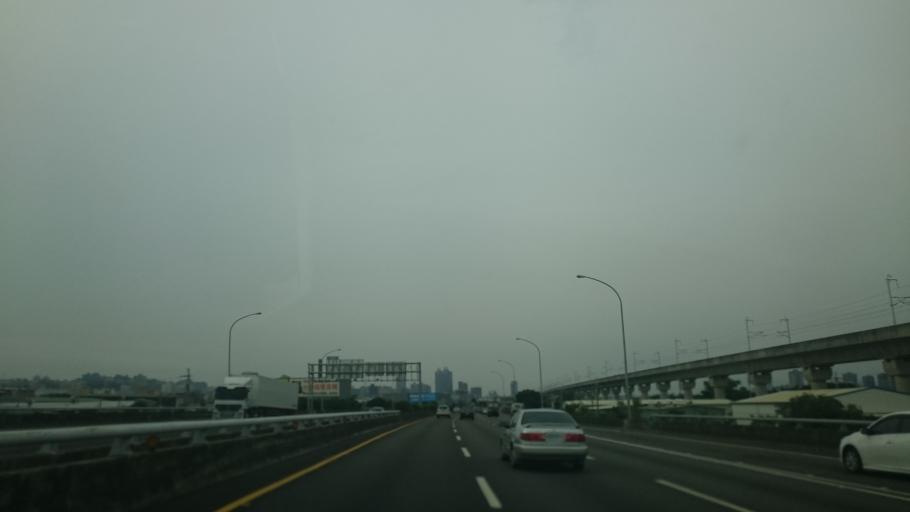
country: TW
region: Taiwan
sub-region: Taichung City
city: Taichung
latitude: 24.1582
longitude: 120.6206
